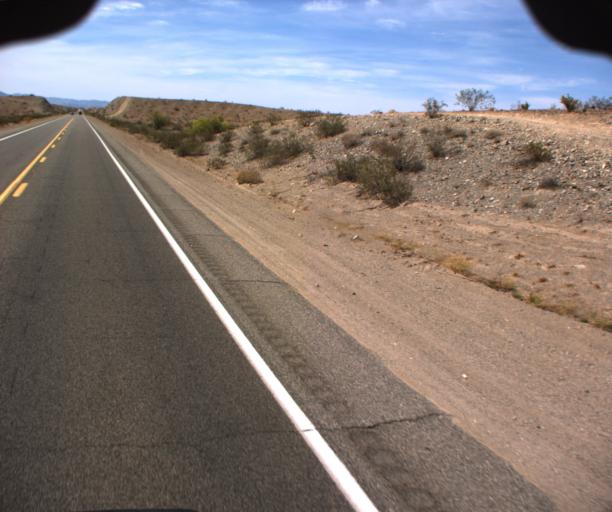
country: US
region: Arizona
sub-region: Mohave County
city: Lake Havasu City
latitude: 34.4296
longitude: -114.2124
